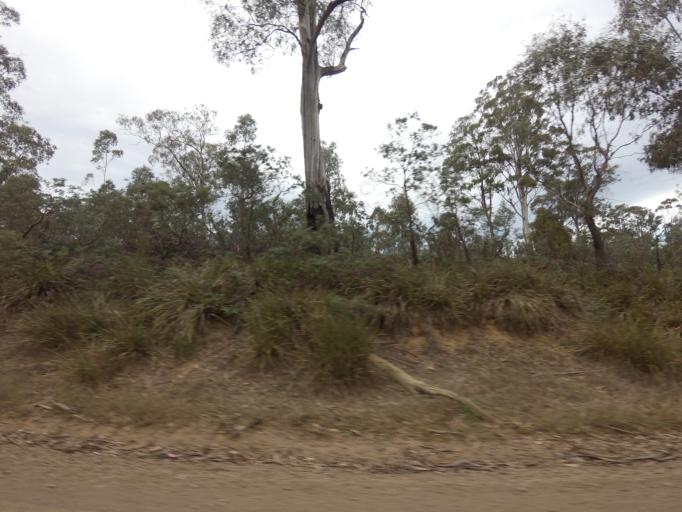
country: AU
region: Tasmania
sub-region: Derwent Valley
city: New Norfolk
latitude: -42.5632
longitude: 146.9396
